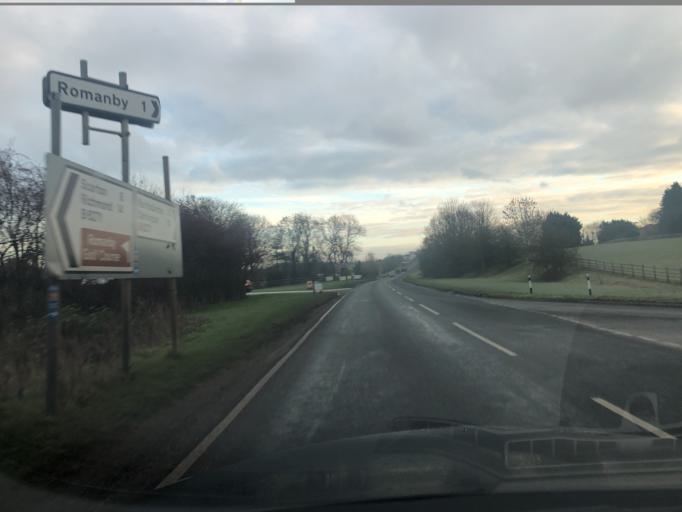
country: GB
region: England
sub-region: North Yorkshire
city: Northallerton
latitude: 54.3446
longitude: -1.4650
